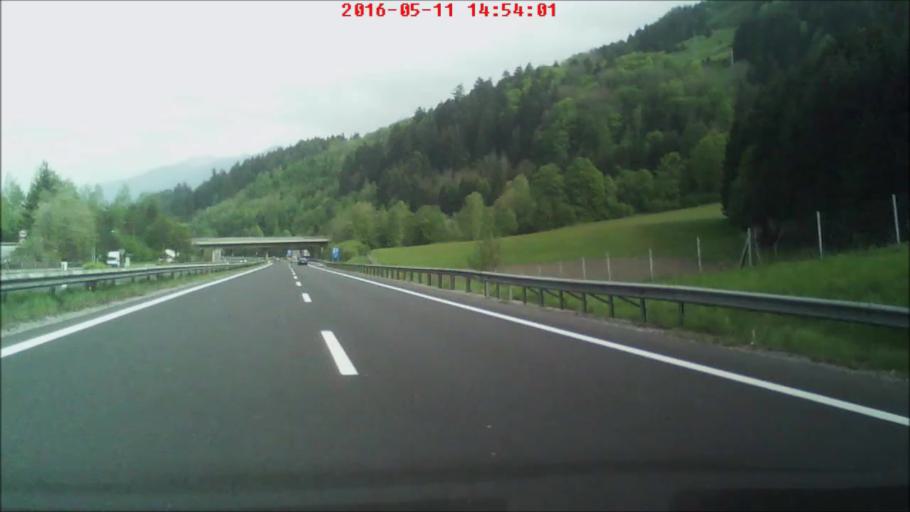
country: AT
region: Styria
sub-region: Politischer Bezirk Liezen
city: Rottenmann
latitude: 47.5192
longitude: 14.3826
